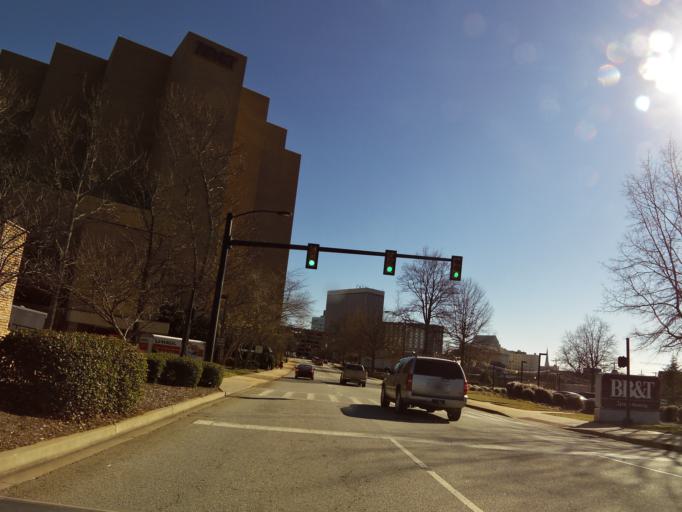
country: US
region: South Carolina
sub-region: Greenville County
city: Greenville
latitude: 34.8555
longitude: -82.4022
